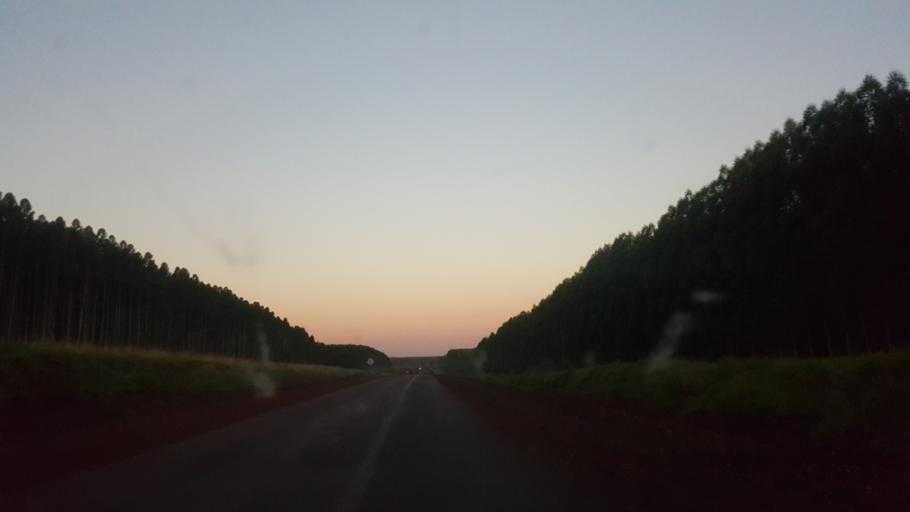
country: AR
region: Corrientes
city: Garruchos
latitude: -28.2475
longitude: -55.8421
